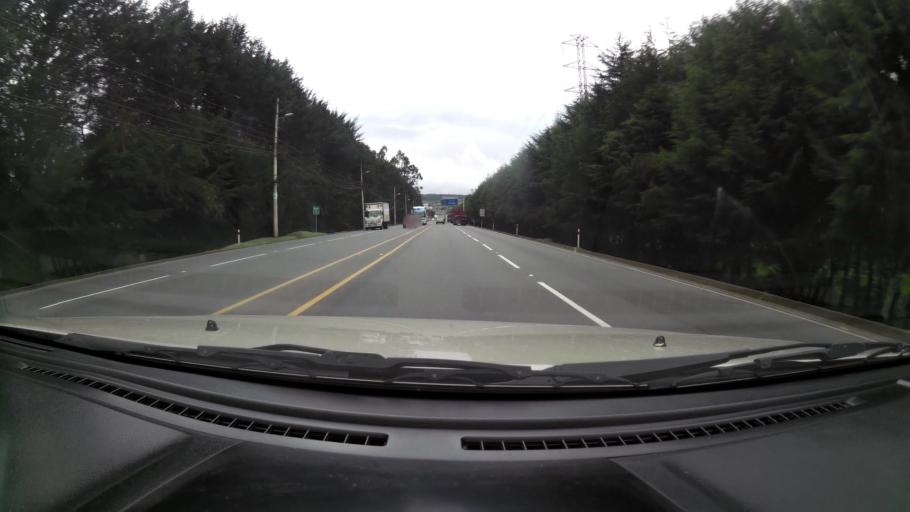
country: EC
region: Pichincha
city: Machachi
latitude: -0.4672
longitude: -78.5854
